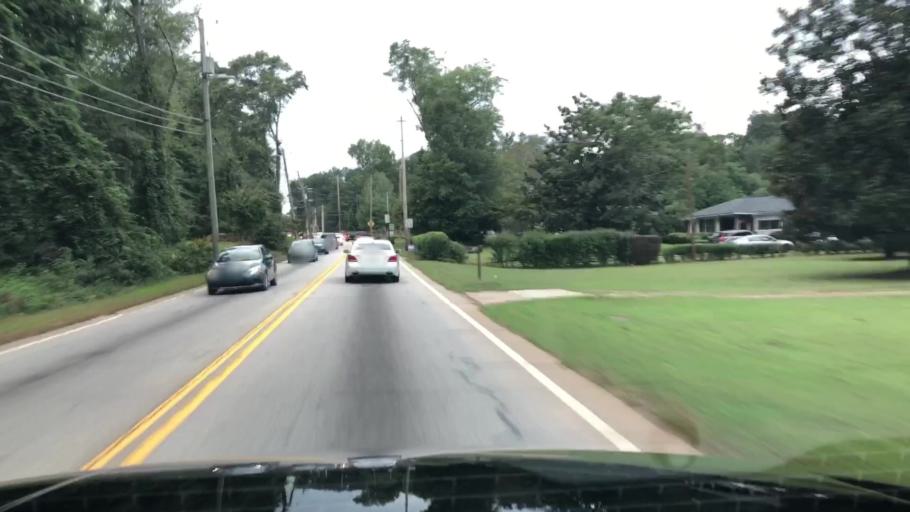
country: US
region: Georgia
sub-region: Fulton County
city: College Park
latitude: 33.6954
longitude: -84.5248
